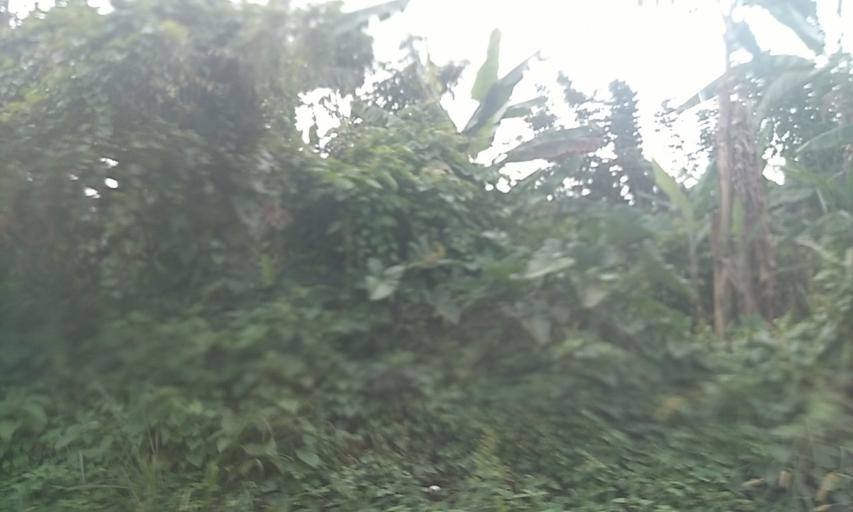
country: UG
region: Central Region
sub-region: Wakiso District
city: Wakiso
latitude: 0.3554
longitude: 32.4606
